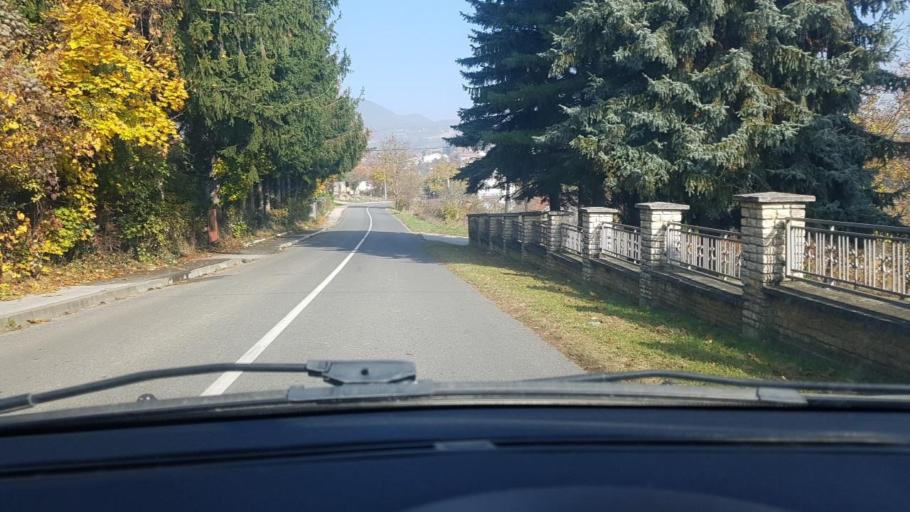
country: HR
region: Krapinsko-Zagorska
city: Zlatar
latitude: 46.1324
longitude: 16.1214
